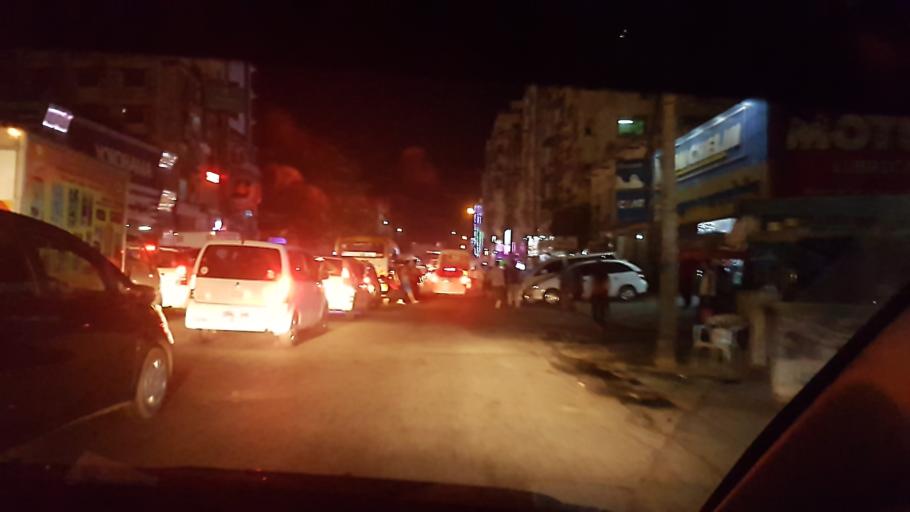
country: MM
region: Yangon
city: Yangon
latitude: 16.8039
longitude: 96.1408
